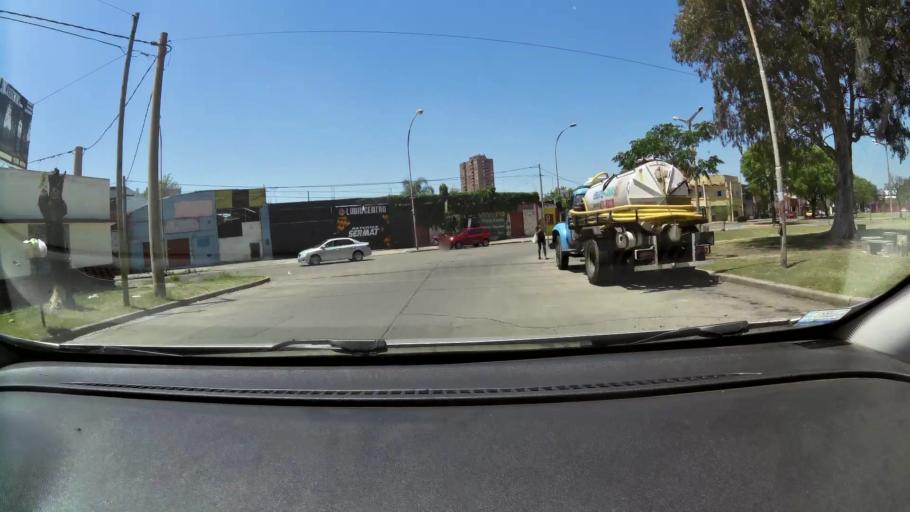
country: AR
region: Cordoba
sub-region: Departamento de Capital
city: Cordoba
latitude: -31.4003
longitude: -64.2108
